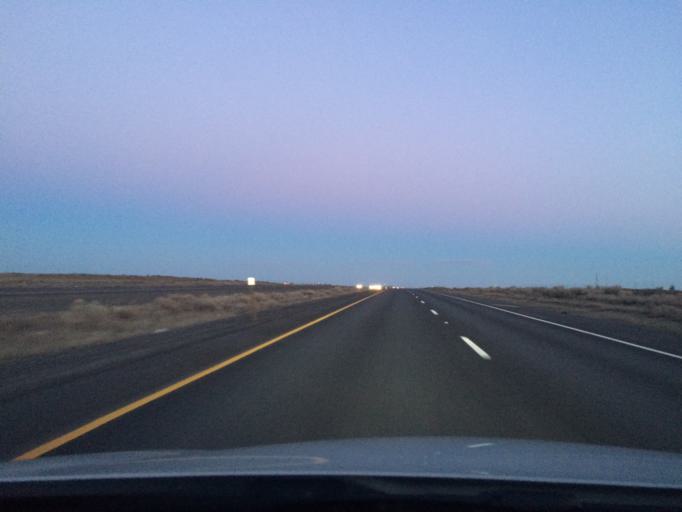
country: US
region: Washington
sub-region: Grant County
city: Royal City
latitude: 47.1036
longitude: -119.6871
